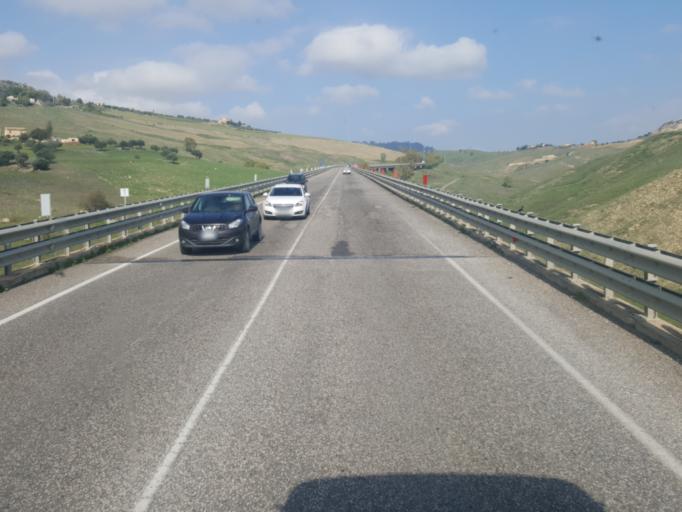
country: IT
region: Sicily
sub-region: Enna
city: Pietraperzia
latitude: 37.4612
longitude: 14.1035
